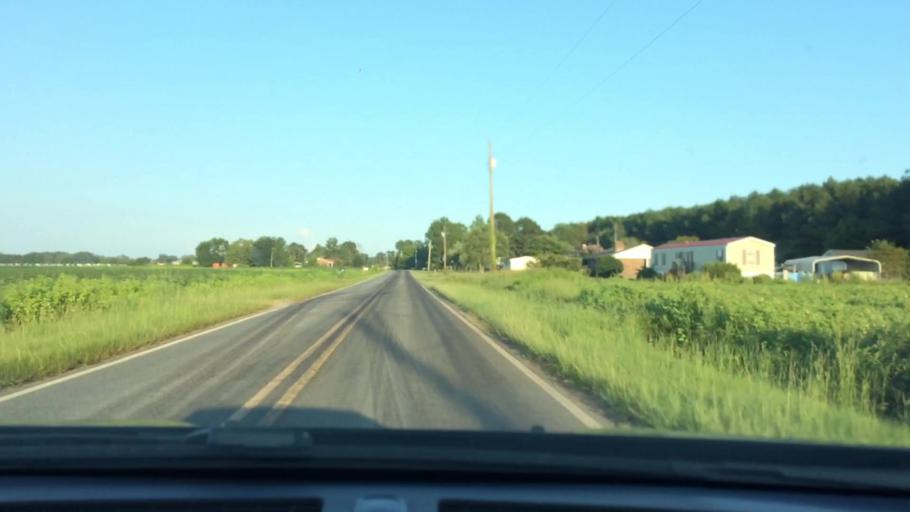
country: US
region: North Carolina
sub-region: Pitt County
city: Ayden
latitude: 35.4315
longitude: -77.4492
